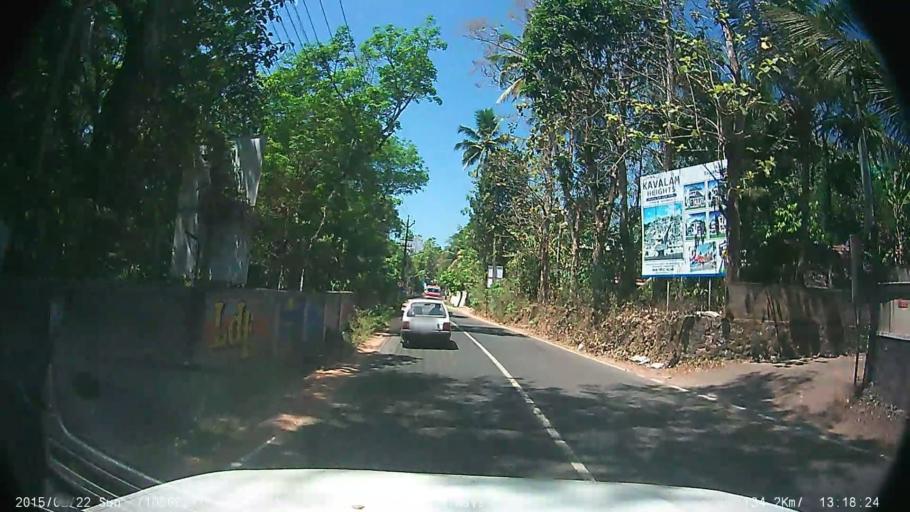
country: IN
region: Kerala
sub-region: Kottayam
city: Changanacheri
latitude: 9.4679
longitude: 76.5785
